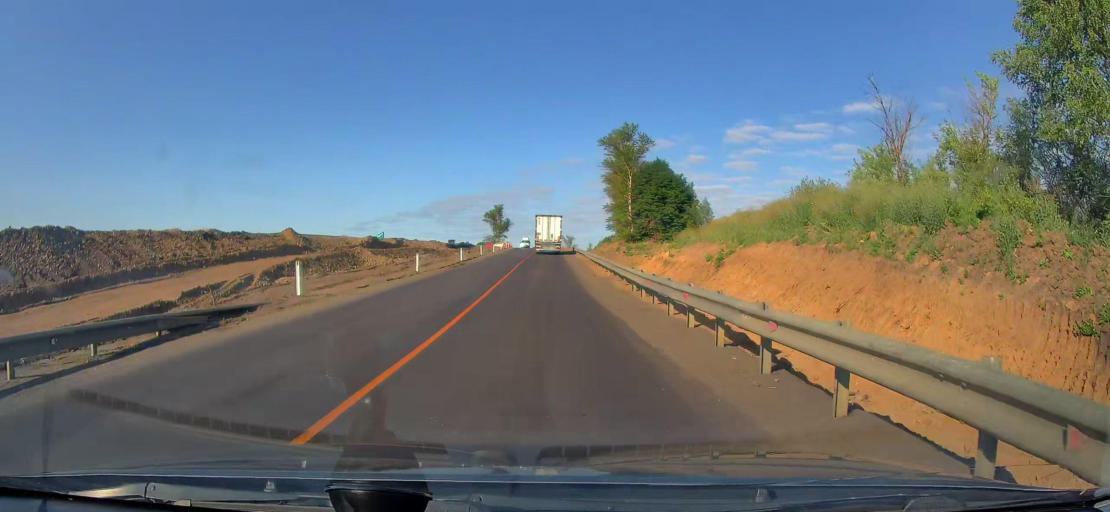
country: RU
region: Tula
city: Bol'shoye Skuratovo
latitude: 53.4440
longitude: 36.8341
